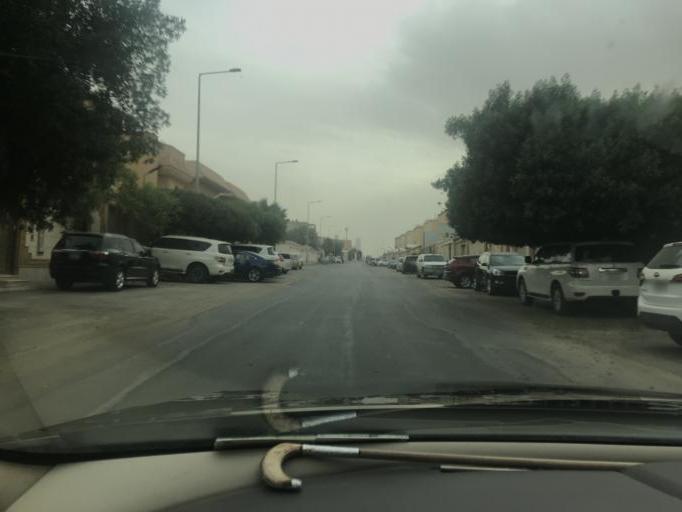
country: SA
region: Ar Riyad
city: Riyadh
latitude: 24.7869
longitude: 46.6969
